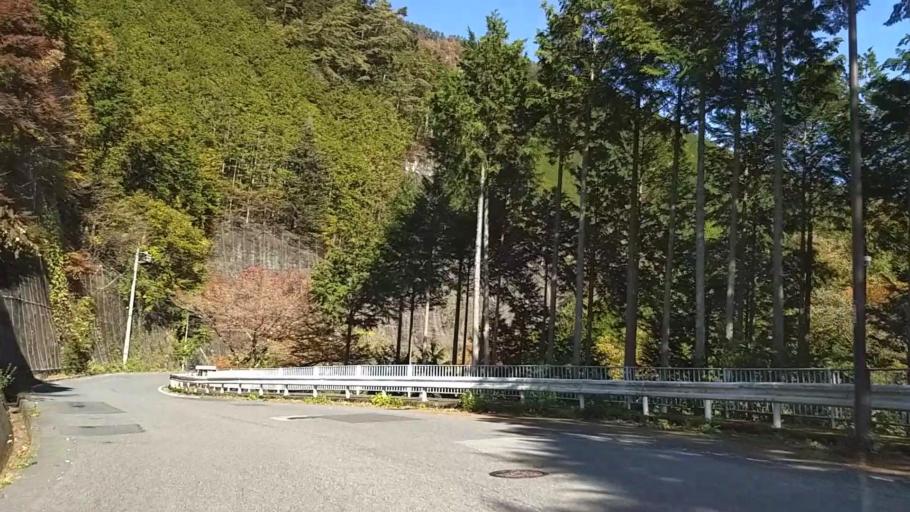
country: JP
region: Yamanashi
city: Otsuki
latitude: 35.7580
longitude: 138.9578
